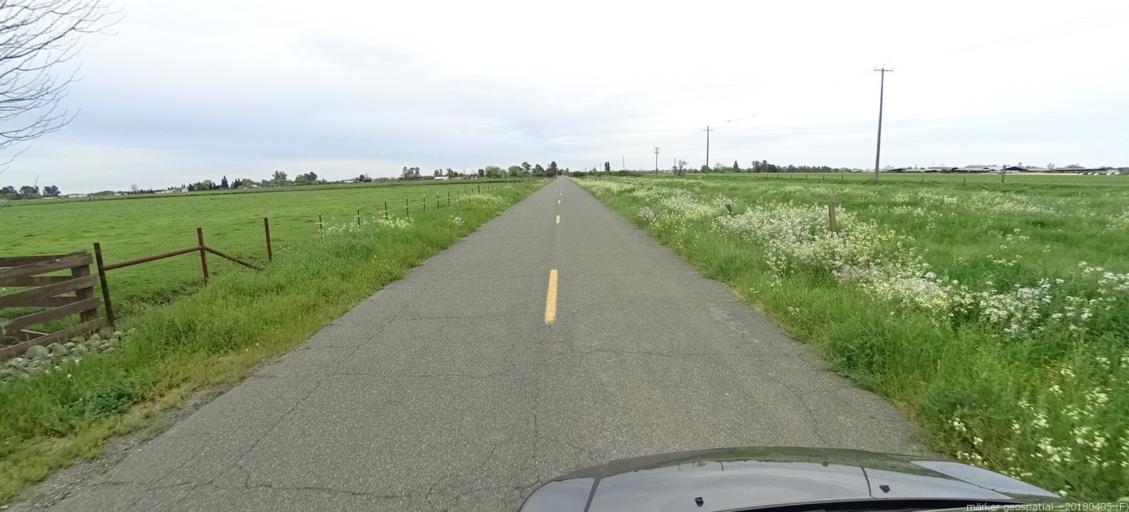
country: US
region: California
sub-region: Sacramento County
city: Herald
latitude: 38.2702
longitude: -121.2445
